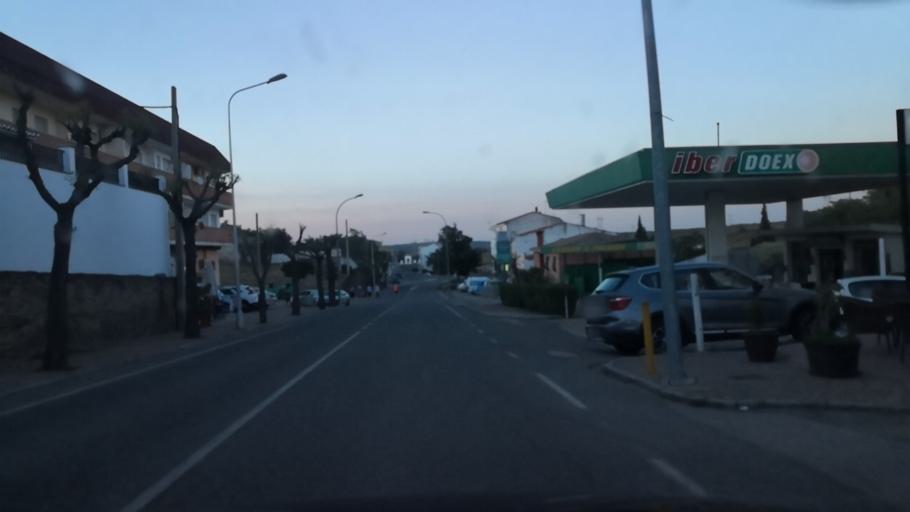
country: ES
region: Extremadura
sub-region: Provincia de Caceres
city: Alcantara
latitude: 39.7142
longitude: -6.8835
